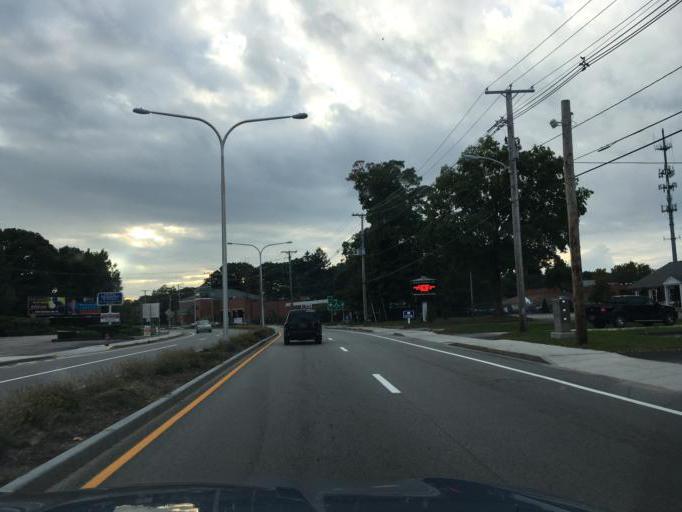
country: US
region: Rhode Island
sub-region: Kent County
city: Warwick
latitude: 41.7026
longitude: -71.4559
